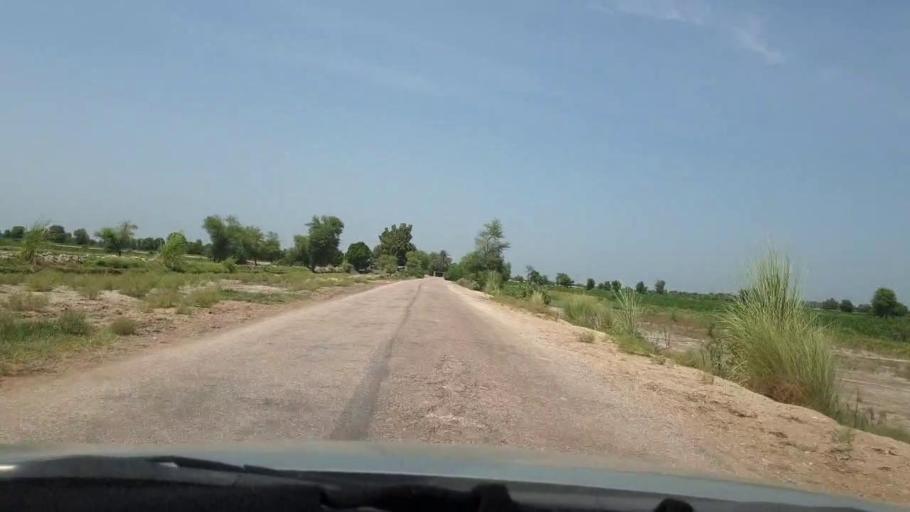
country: PK
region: Sindh
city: Pano Aqil
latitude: 27.6668
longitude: 69.1082
